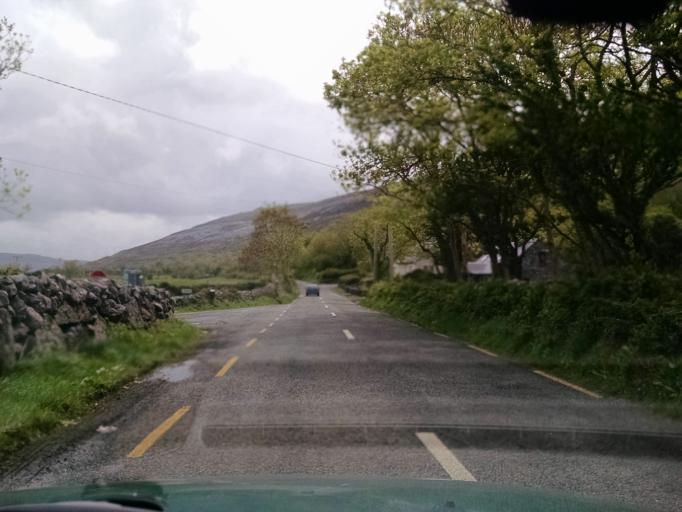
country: IE
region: Connaught
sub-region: County Galway
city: Bearna
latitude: 53.1395
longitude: -9.2237
